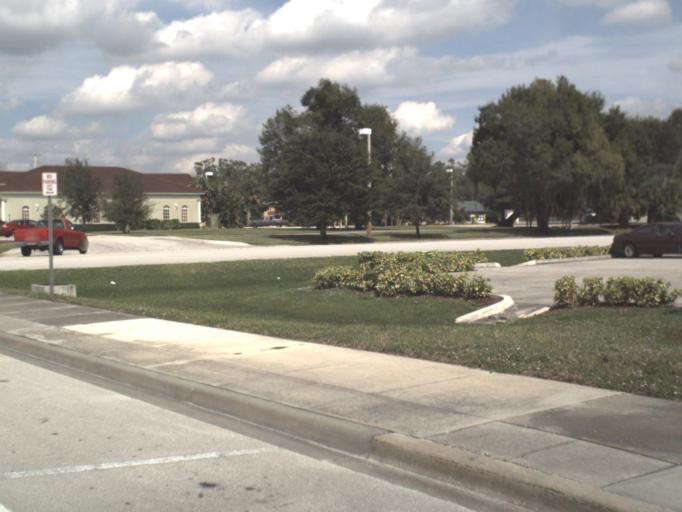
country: US
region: Florida
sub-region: Okeechobee County
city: Okeechobee
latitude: 27.2476
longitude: -80.8298
